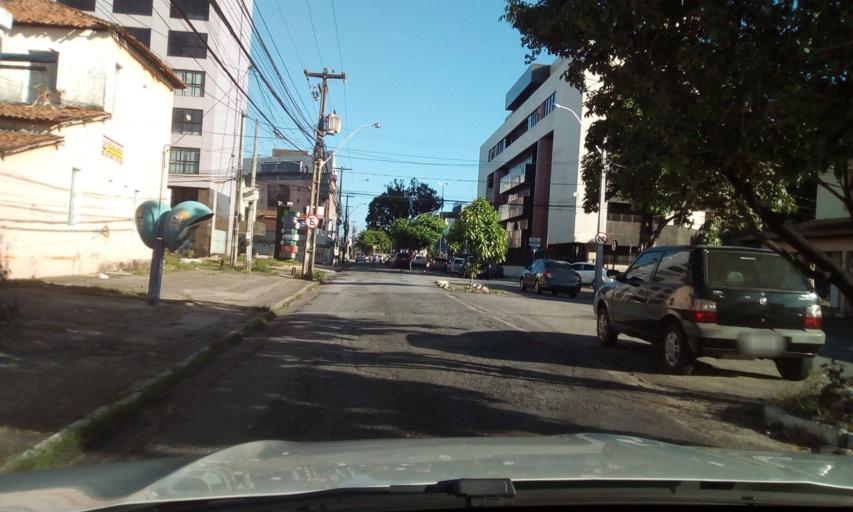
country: BR
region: Paraiba
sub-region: Joao Pessoa
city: Joao Pessoa
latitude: -7.1210
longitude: -34.8726
